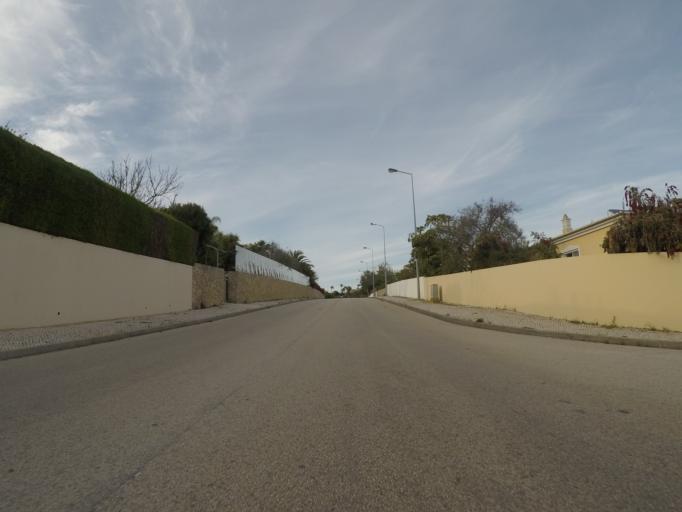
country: PT
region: Faro
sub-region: Lagos
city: Lagos
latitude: 37.0895
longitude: -8.7364
